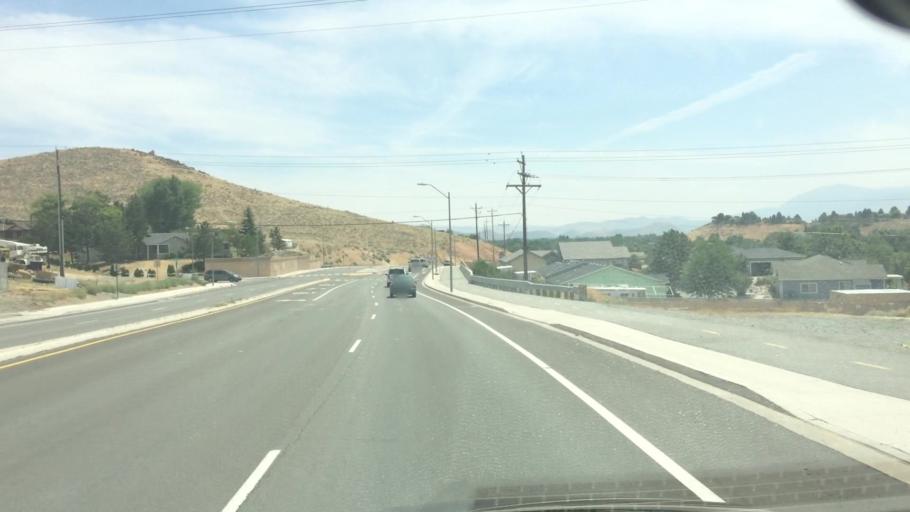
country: US
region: Nevada
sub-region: Washoe County
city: Sparks
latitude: 39.5710
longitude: -119.7243
